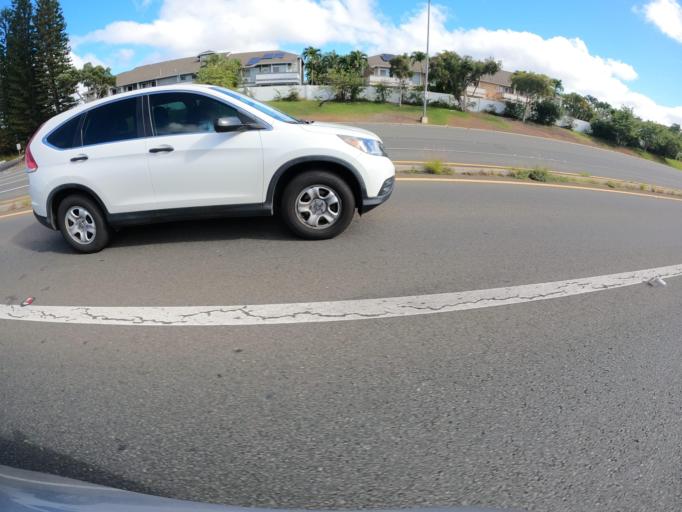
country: US
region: Hawaii
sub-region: Honolulu County
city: Halawa
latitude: 21.3677
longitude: -157.9248
